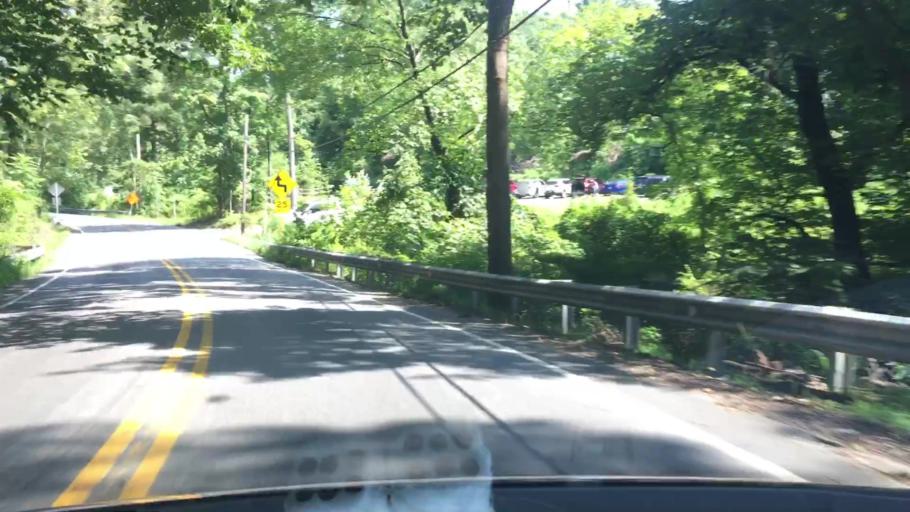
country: US
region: Pennsylvania
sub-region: Delaware County
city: Village Green-Green Ridge
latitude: 39.8762
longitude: -75.4172
